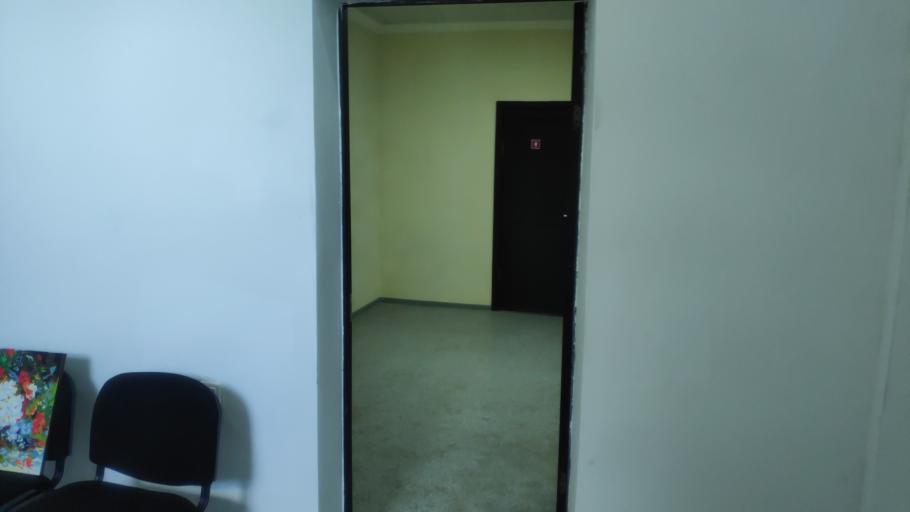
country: KZ
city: Priozersk
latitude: 46.0343
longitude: 73.7006
